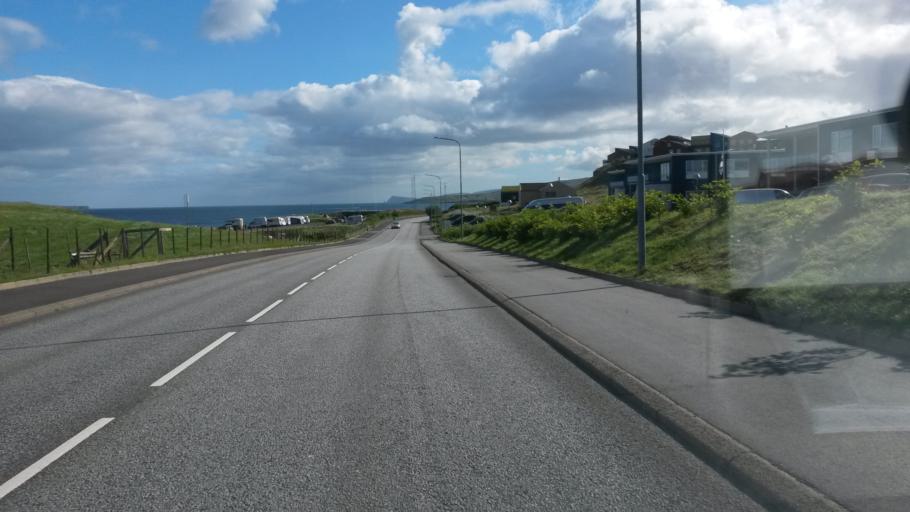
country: FO
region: Streymoy
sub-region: Torshavn
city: Torshavn
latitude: 62.0190
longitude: -6.7567
